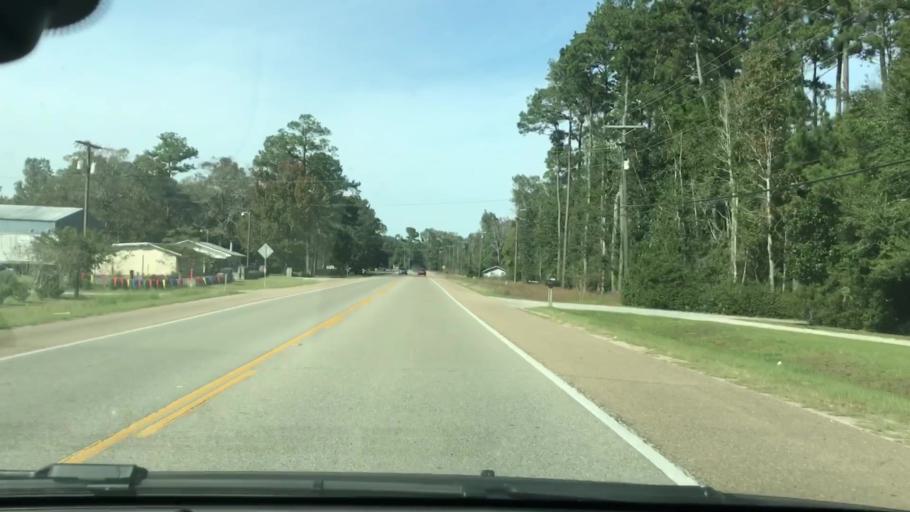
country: US
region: Louisiana
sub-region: Saint Tammany Parish
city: Pearl River
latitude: 30.3998
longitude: -89.7632
